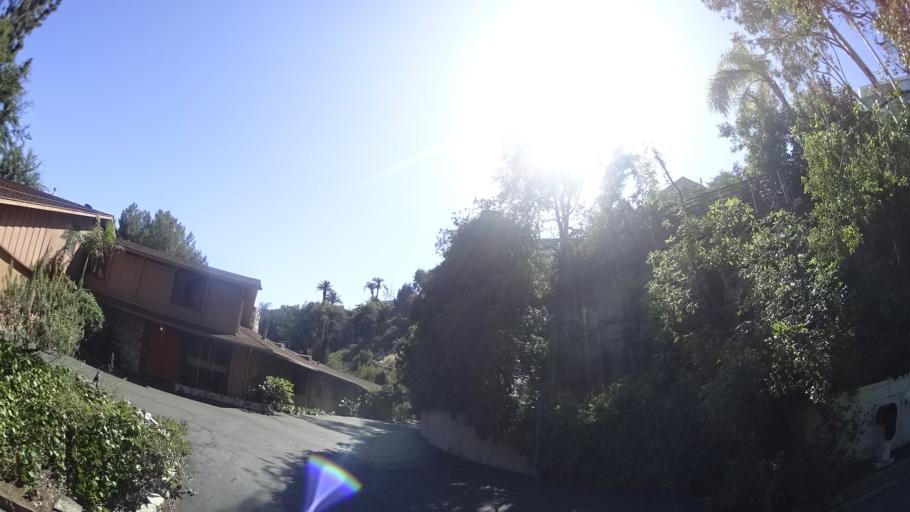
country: US
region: California
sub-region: Los Angeles County
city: Beverly Hills
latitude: 34.0957
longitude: -118.3886
